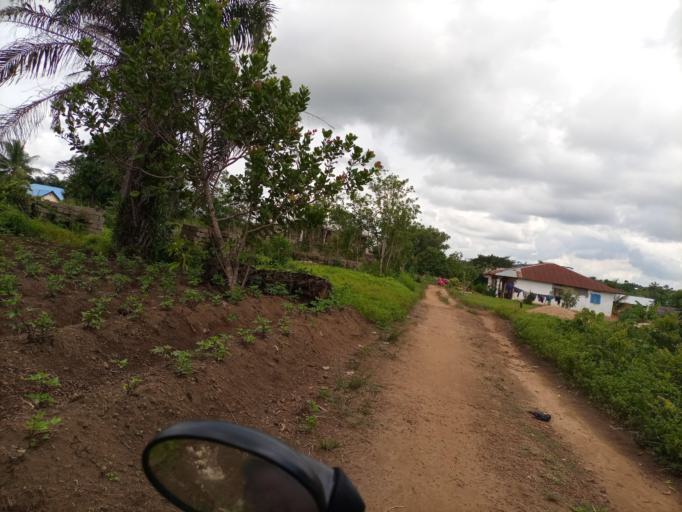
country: SL
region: Southern Province
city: Bo
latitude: 7.9727
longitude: -11.7664
